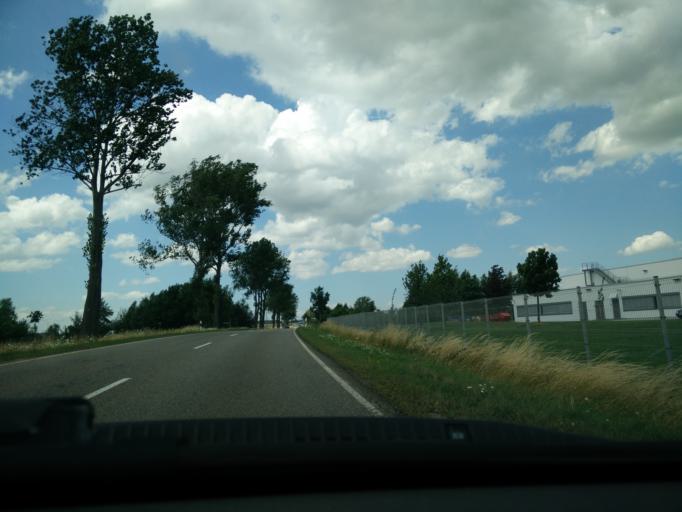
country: DE
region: Saxony
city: Wittgensdorf
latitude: 50.8658
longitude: 12.8487
